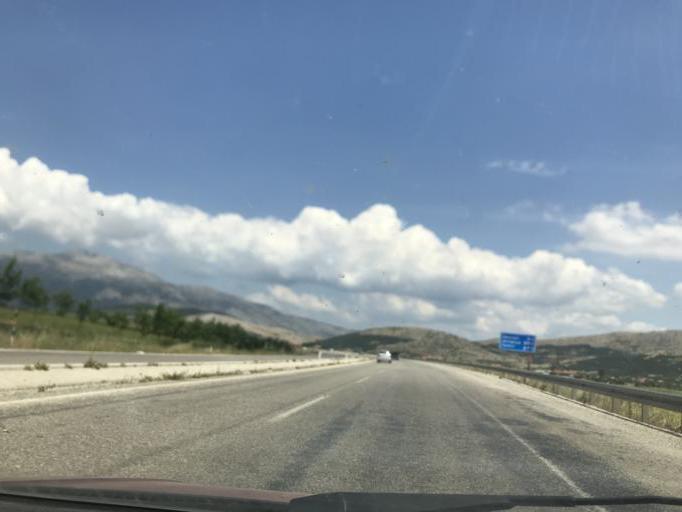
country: TR
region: Denizli
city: Serinhisar
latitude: 37.6163
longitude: 29.1799
